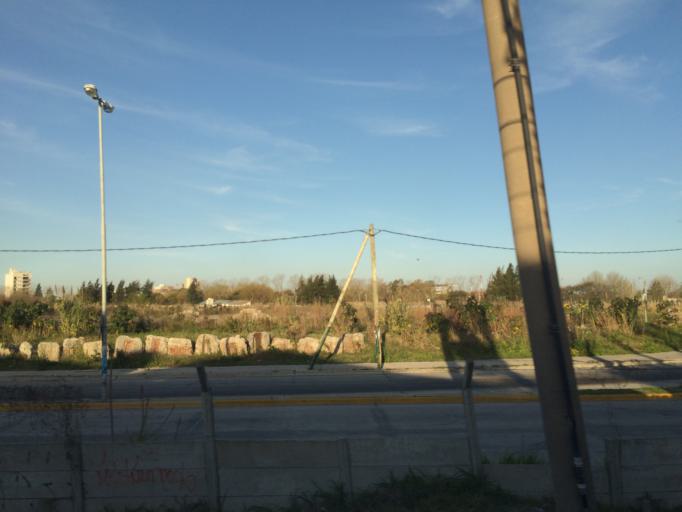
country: AR
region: Buenos Aires
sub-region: Partido de Lanus
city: Lanus
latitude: -34.7160
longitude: -58.3923
